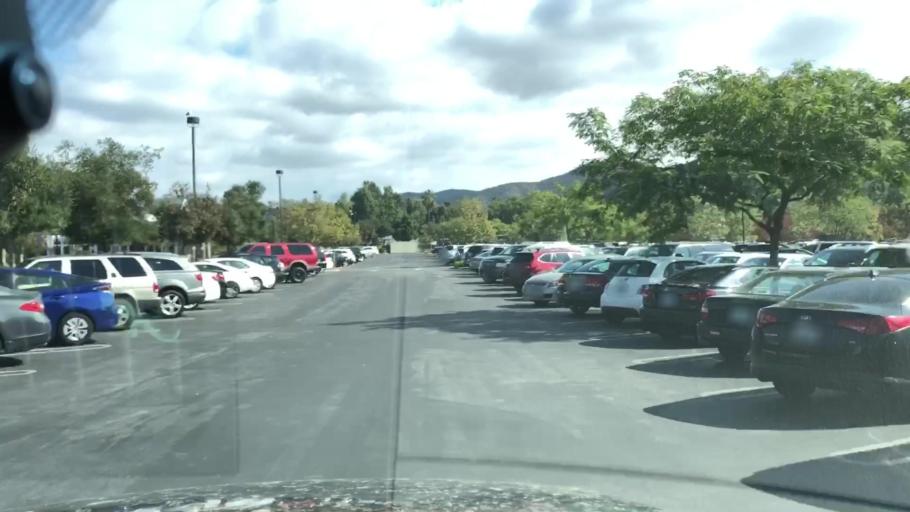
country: US
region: California
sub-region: Ventura County
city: Thousand Oaks
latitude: 34.1818
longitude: -118.8841
